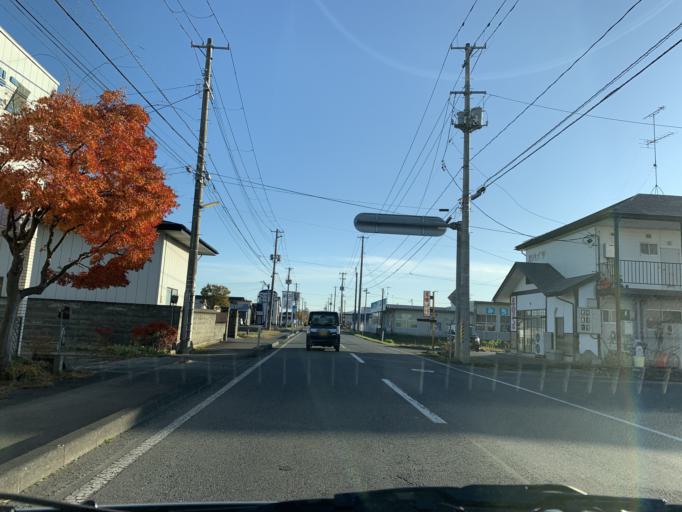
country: JP
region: Iwate
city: Mizusawa
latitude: 39.1814
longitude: 141.1765
